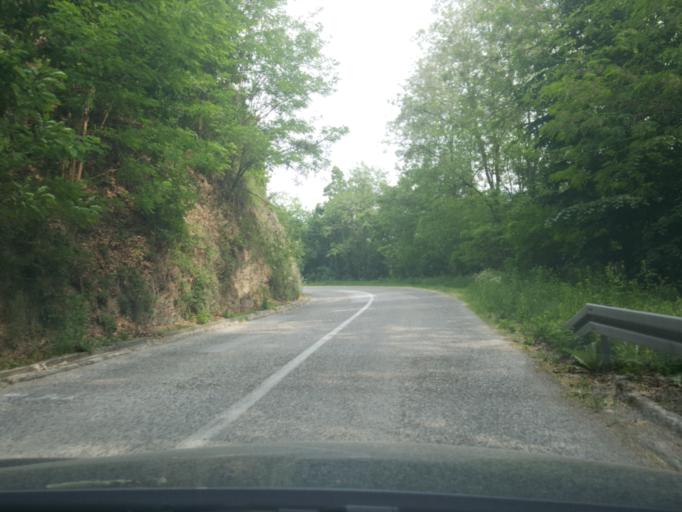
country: RS
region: Central Serbia
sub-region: Zlatiborski Okrug
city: Bajina Basta
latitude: 44.0427
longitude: 19.6250
